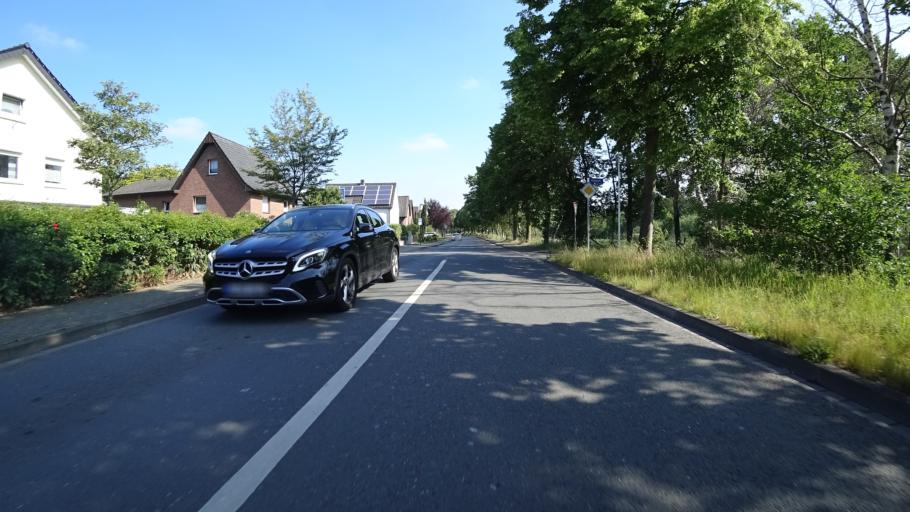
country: DE
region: North Rhine-Westphalia
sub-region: Regierungsbezirk Arnsberg
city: Lippstadt
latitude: 51.6724
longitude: 8.3827
